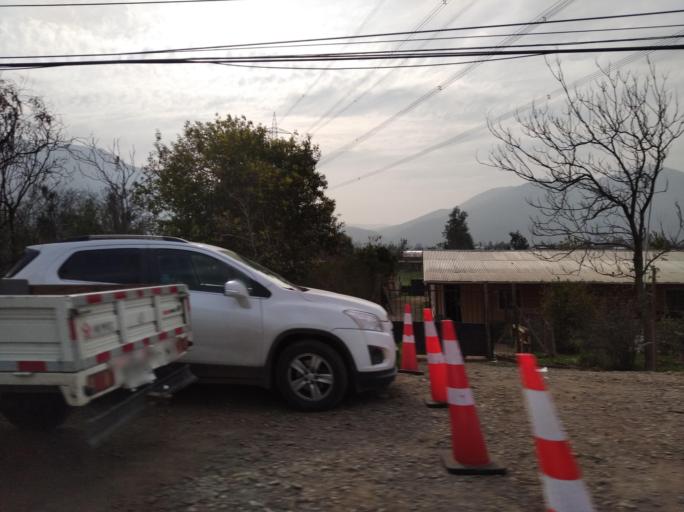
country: CL
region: Santiago Metropolitan
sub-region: Provincia de Chacabuco
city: Lampa
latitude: -33.2641
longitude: -70.8968
